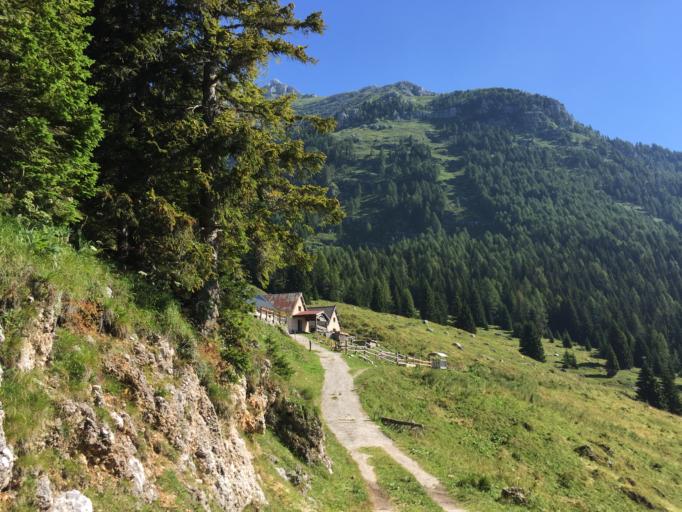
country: SI
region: Bovec
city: Bovec
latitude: 46.4000
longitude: 13.4782
